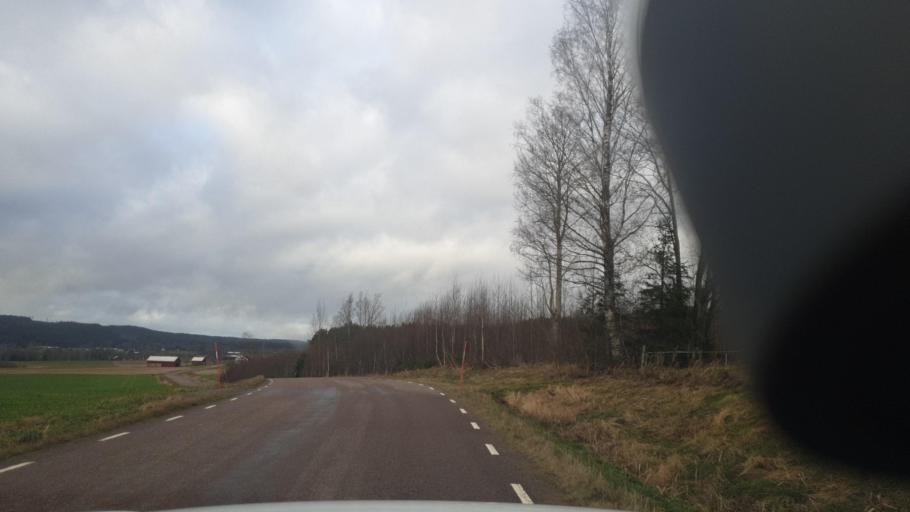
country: SE
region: Vaermland
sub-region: Sunne Kommun
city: Sunne
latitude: 59.7401
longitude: 13.1032
